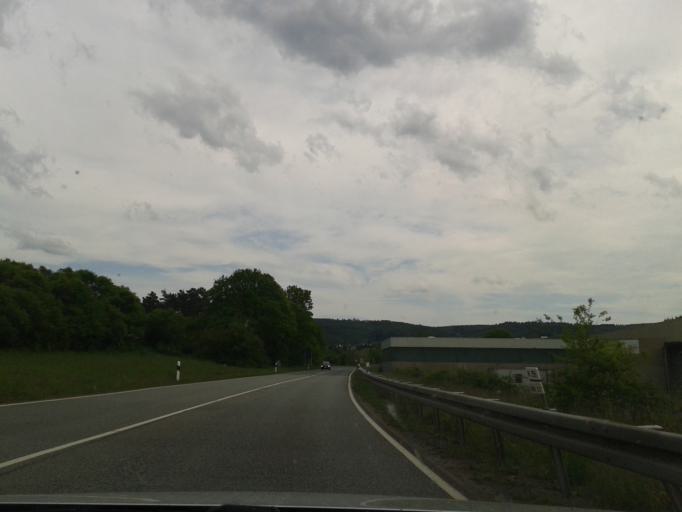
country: DE
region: Hesse
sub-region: Regierungsbezirk Giessen
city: Mittenaar
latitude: 50.6960
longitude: 8.3534
